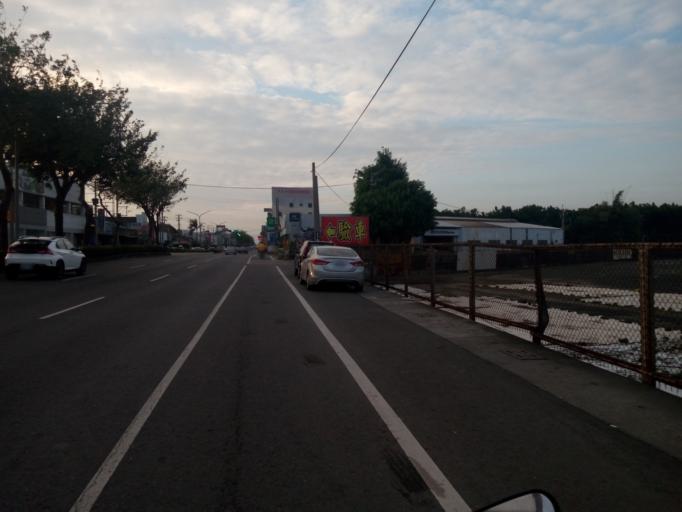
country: TW
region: Taiwan
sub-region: Chiayi
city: Jiayi Shi
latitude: 23.4857
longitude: 120.4191
